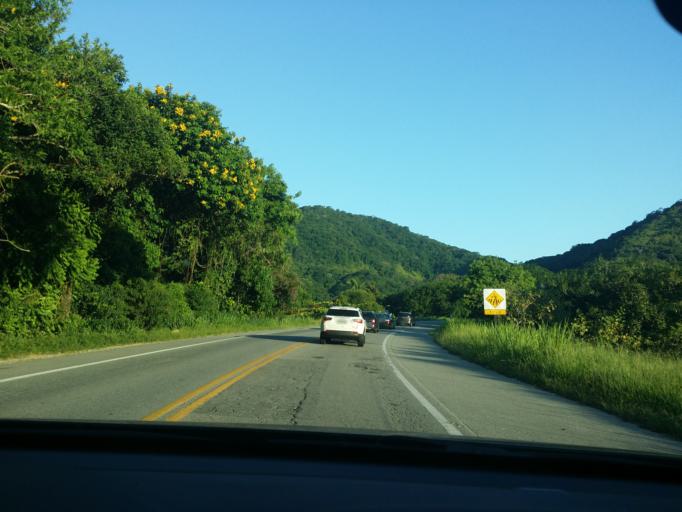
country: BR
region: Sao Paulo
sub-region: Sao Sebastiao
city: Sao Sebastiao
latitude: -23.7688
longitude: -45.6408
